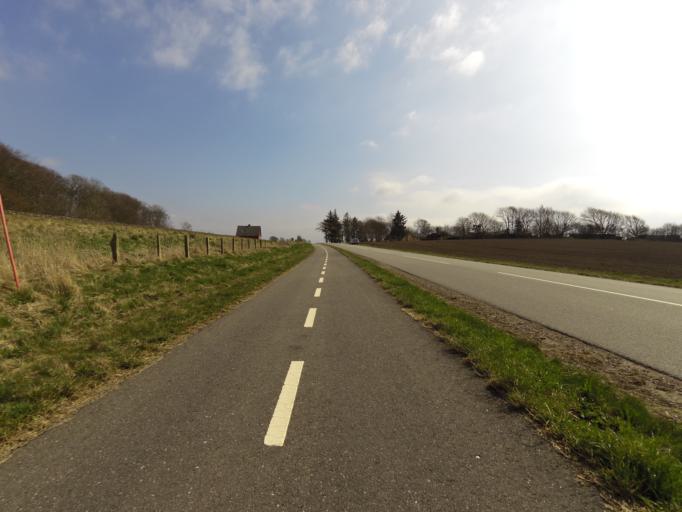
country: DK
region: Central Jutland
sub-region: Struer Kommune
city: Struer
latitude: 56.4505
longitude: 8.6203
